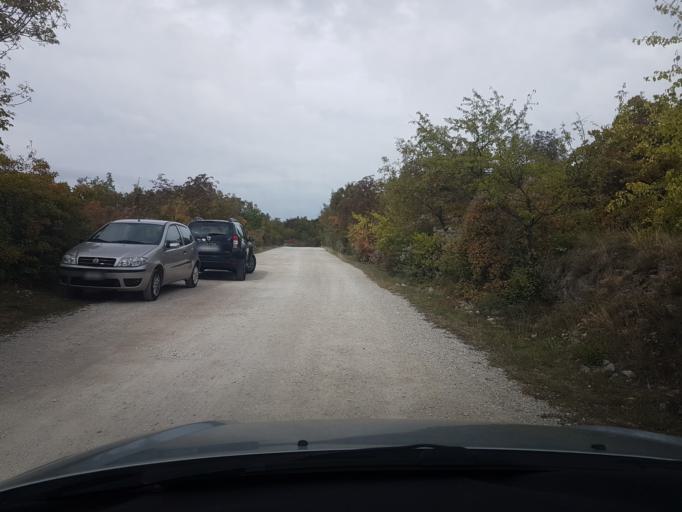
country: IT
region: Friuli Venezia Giulia
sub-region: Provincia di Gorizia
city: Doberdo del Lago
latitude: 45.8429
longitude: 13.5471
